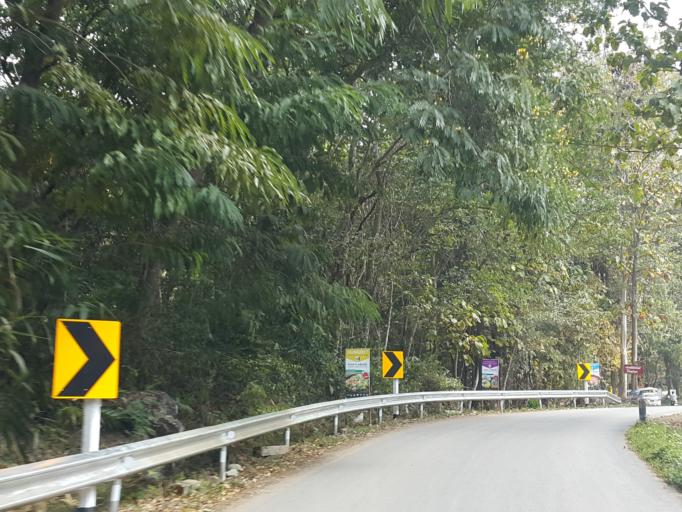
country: TH
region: Chiang Mai
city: Mae On
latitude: 18.8676
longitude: 99.3085
